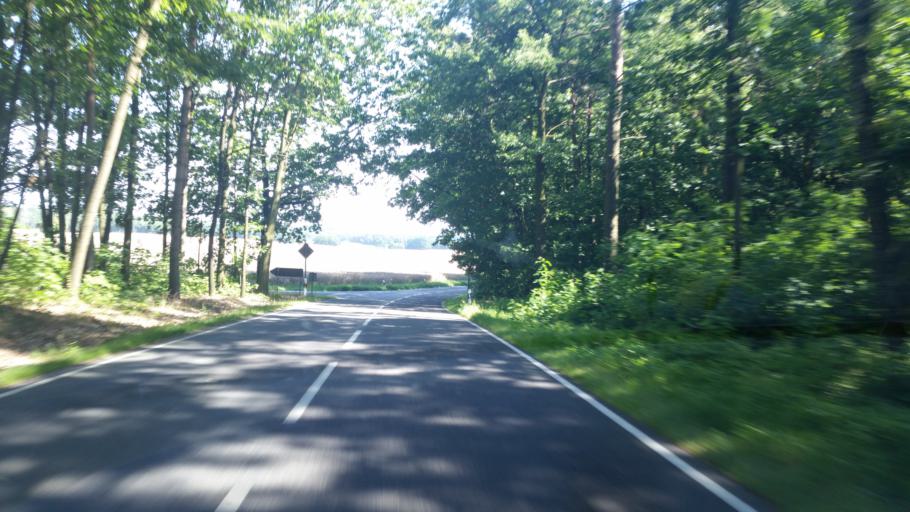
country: DE
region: Saxony
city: Kamenz
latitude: 51.2999
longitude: 14.0498
